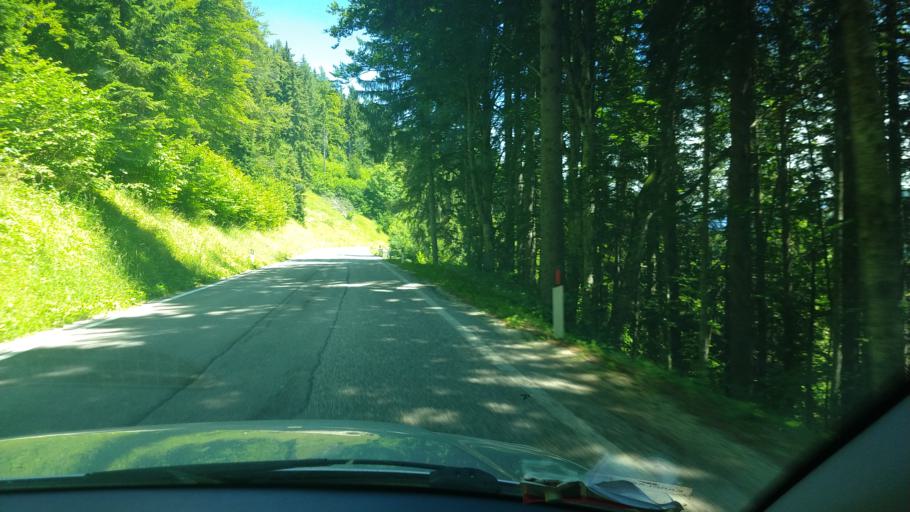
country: IT
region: Trentino-Alto Adige
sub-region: Provincia di Trento
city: Folgaria
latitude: 45.9089
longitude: 11.2062
